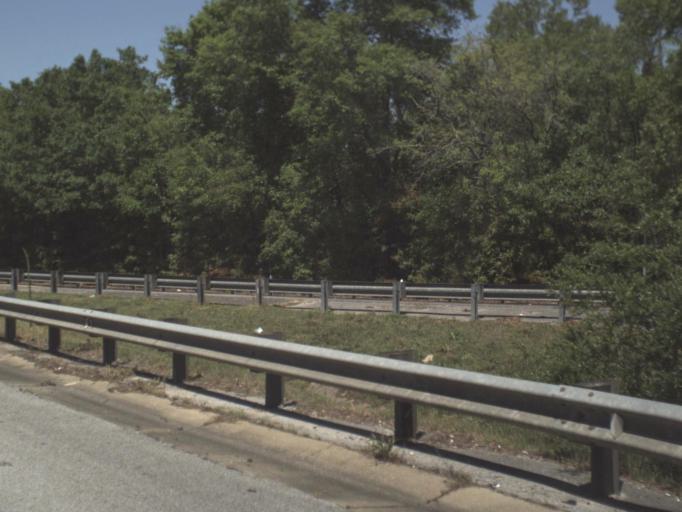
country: US
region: Florida
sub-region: Escambia County
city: Ensley
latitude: 30.5045
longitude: -87.2709
